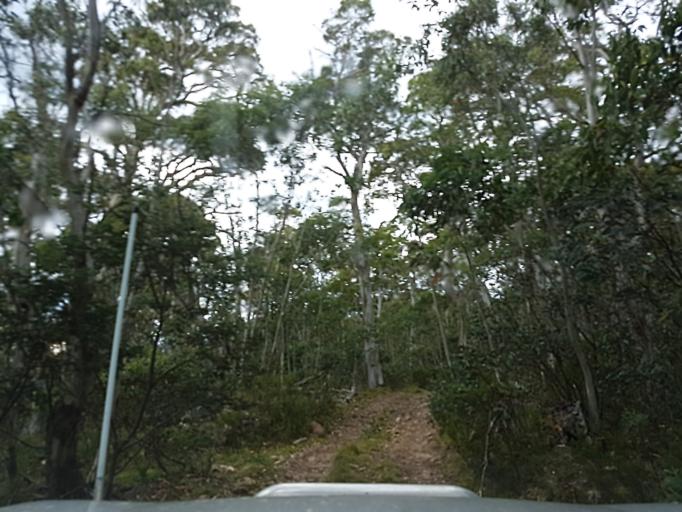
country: AU
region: New South Wales
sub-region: Snowy River
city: Jindabyne
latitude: -36.8817
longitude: 148.1578
